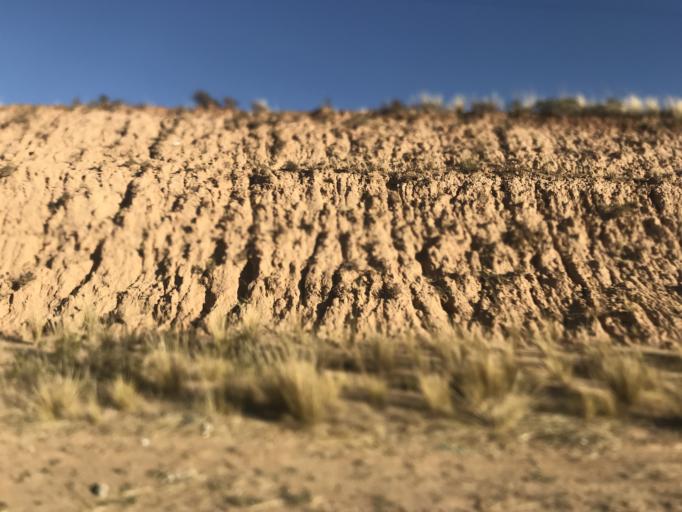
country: BO
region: La Paz
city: Tiahuanaco
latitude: -16.5641
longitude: -68.6332
